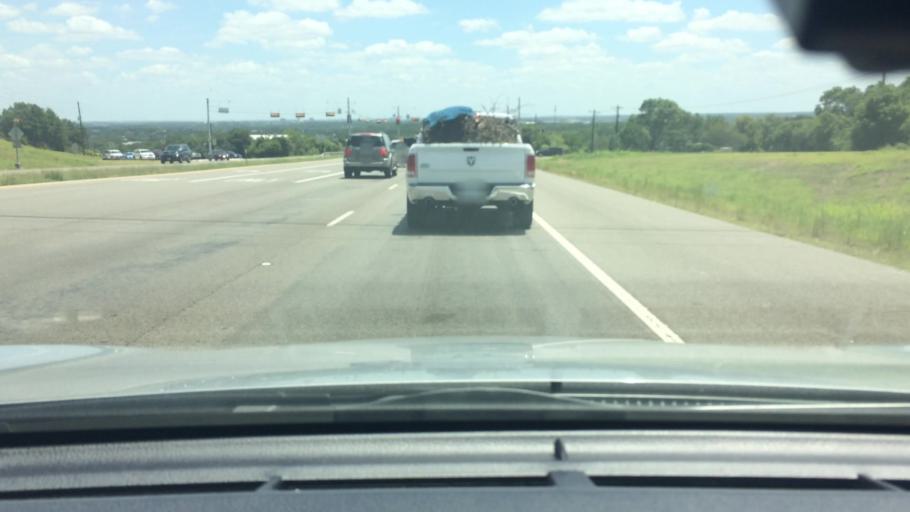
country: US
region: Texas
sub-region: Travis County
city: West Lake Hills
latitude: 30.2785
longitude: -97.8206
